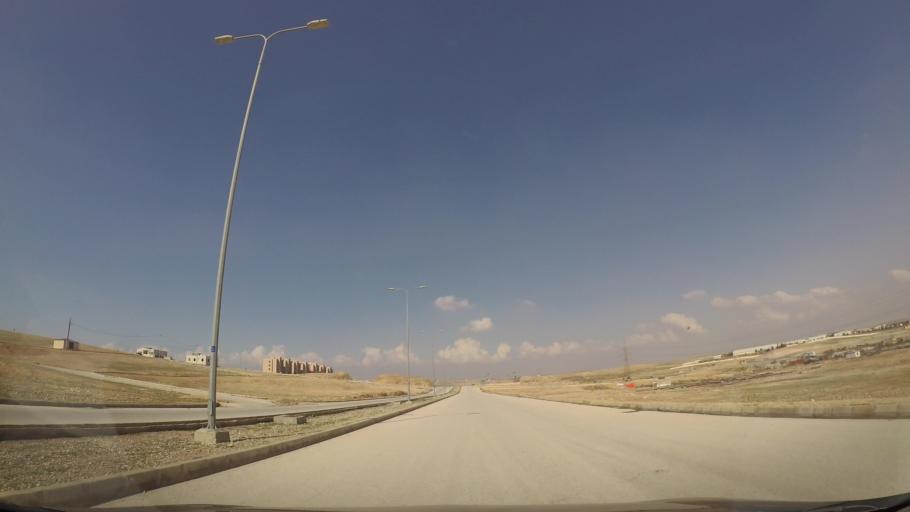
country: JO
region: Zarqa
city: Zarqa
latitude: 32.0524
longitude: 36.1239
